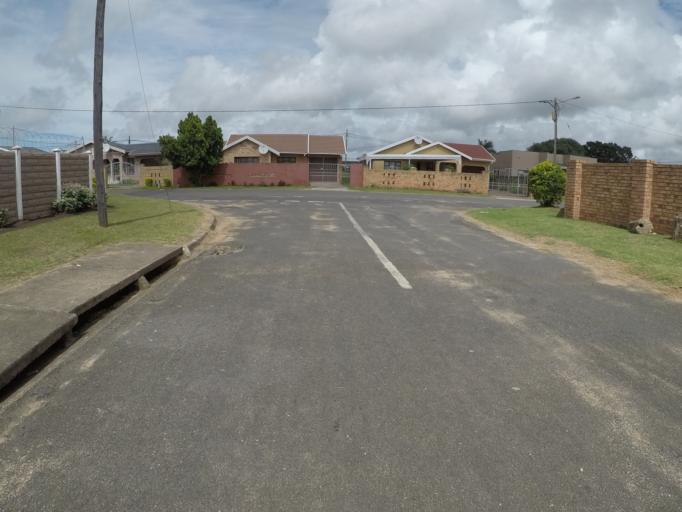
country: ZA
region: KwaZulu-Natal
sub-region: uThungulu District Municipality
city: eSikhawini
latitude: -28.8635
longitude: 31.9147
